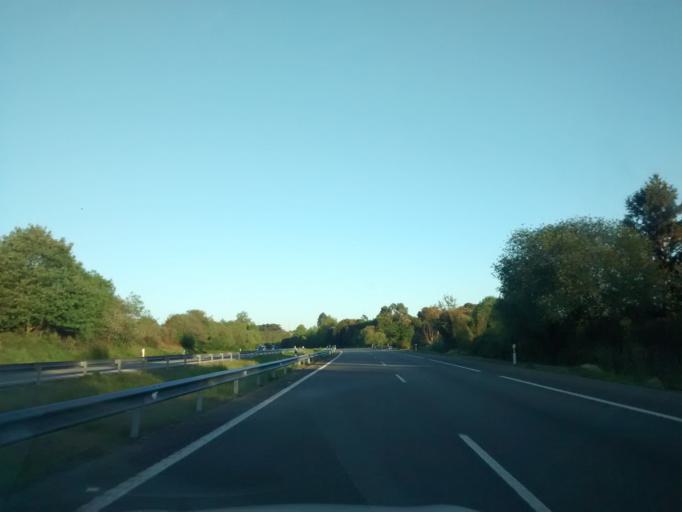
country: ES
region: Asturias
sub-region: Province of Asturias
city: Carrena
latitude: 43.4446
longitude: -4.9148
